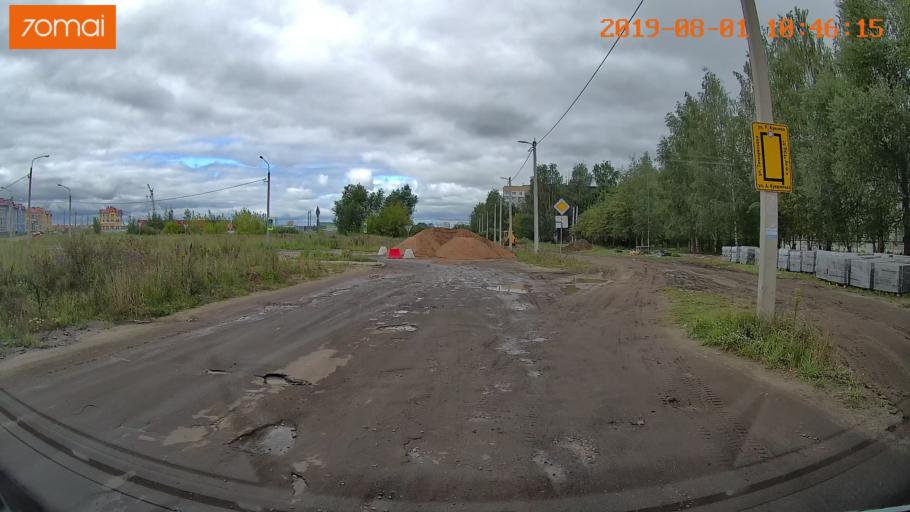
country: RU
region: Ivanovo
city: Kokhma
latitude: 56.9518
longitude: 41.1045
